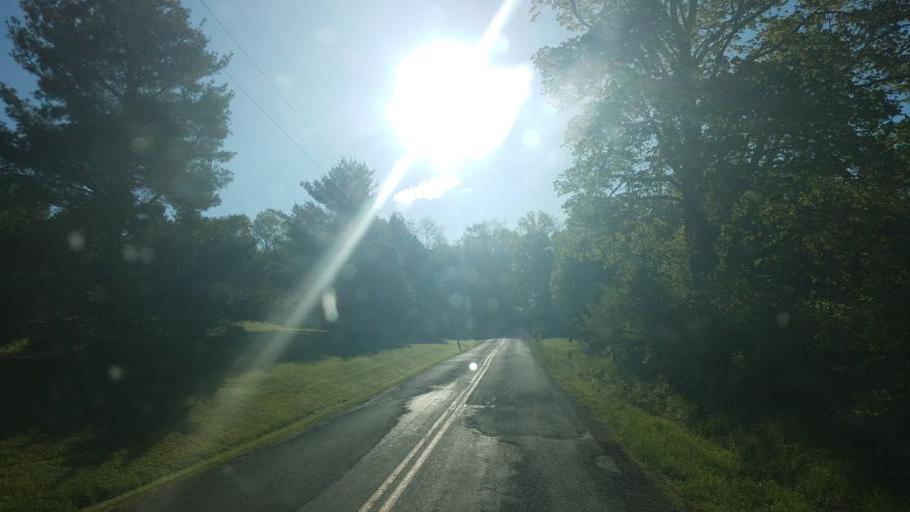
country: US
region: Ohio
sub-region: Sandusky County
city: Bellville
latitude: 40.5397
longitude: -82.4590
